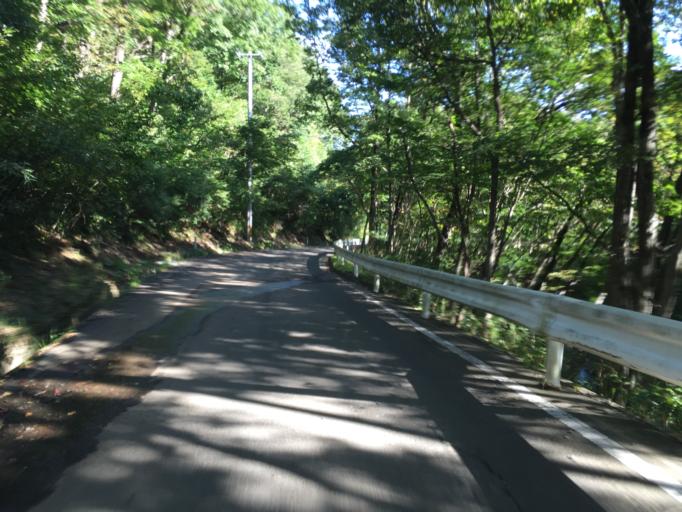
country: JP
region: Fukushima
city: Yanagawamachi-saiwaicho
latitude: 37.8314
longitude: 140.7005
